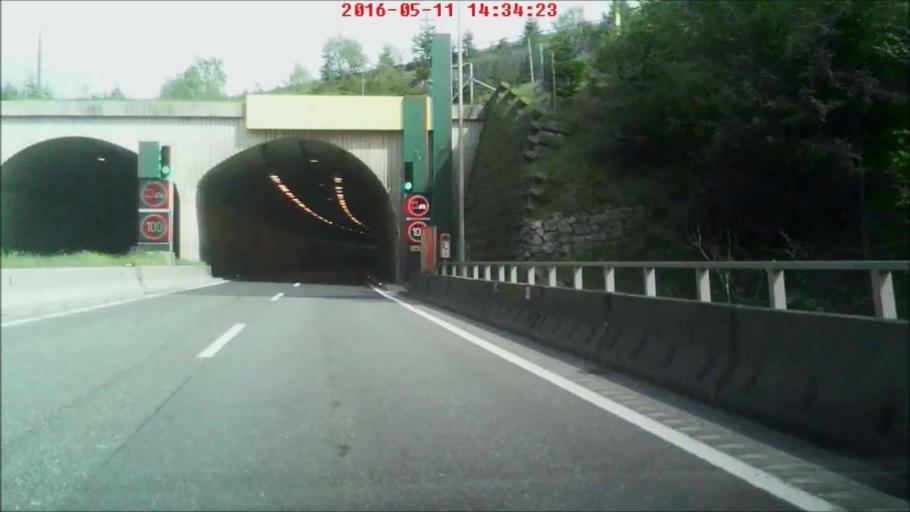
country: AT
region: Upper Austria
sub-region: Politischer Bezirk Kirchdorf an der Krems
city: Rossleithen
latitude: 47.7502
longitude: 14.2511
